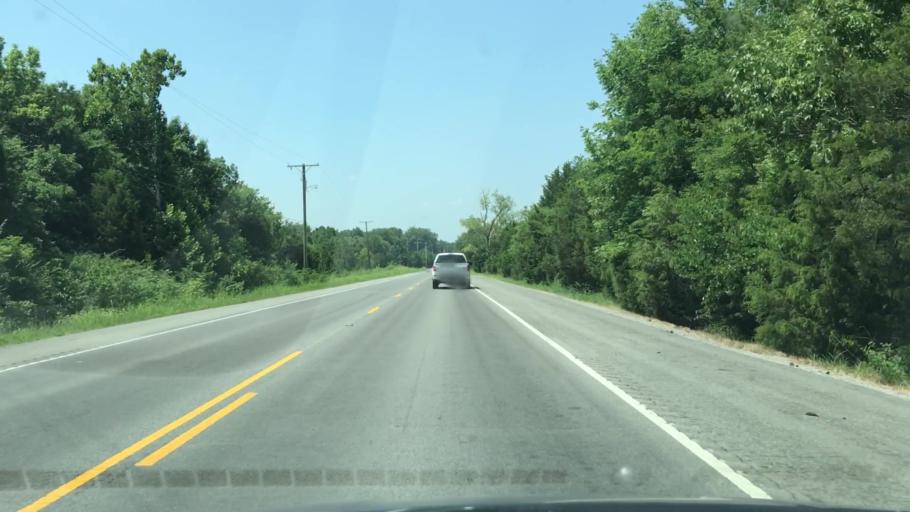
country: US
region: Tennessee
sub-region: Rutherford County
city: La Vergne
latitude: 36.0795
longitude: -86.5690
